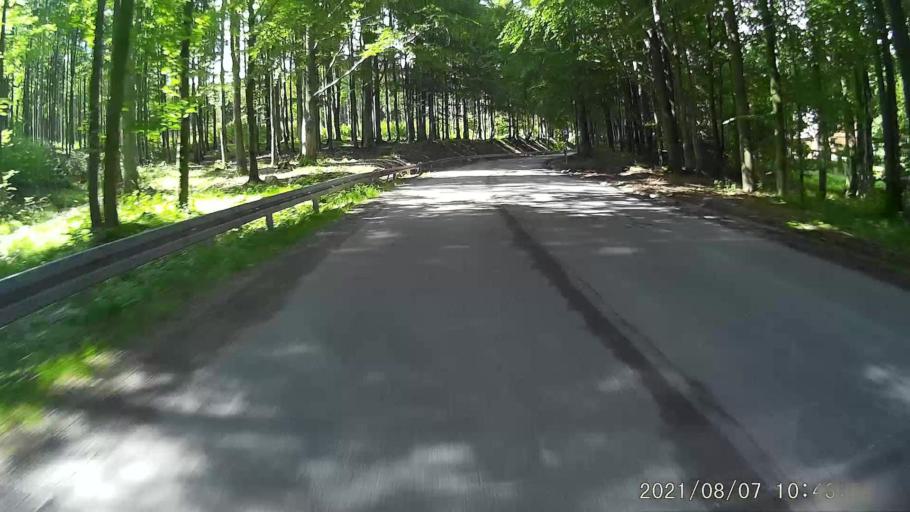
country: PL
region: Lower Silesian Voivodeship
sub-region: Powiat klodzki
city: Duszniki-Zdroj
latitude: 50.3274
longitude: 16.4019
